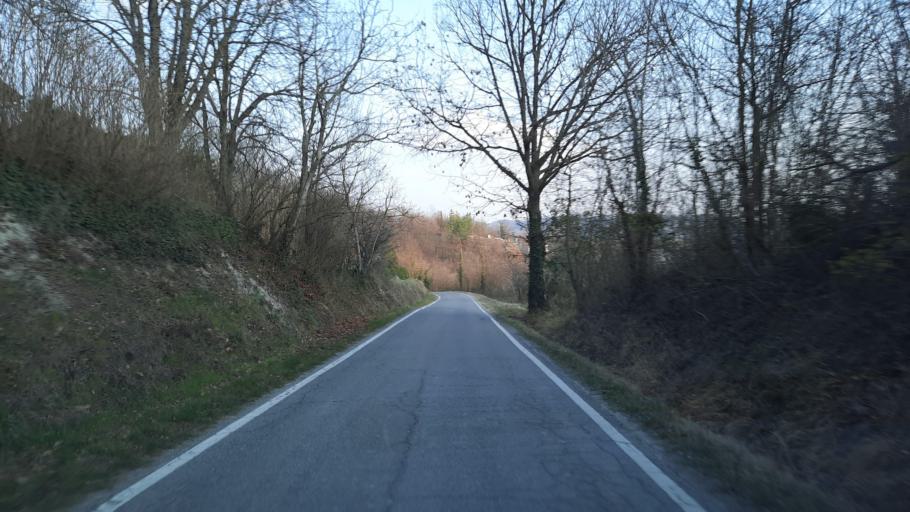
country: IT
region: Piedmont
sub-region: Provincia di Alessandria
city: Odalengo Grande
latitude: 45.1046
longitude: 8.1723
